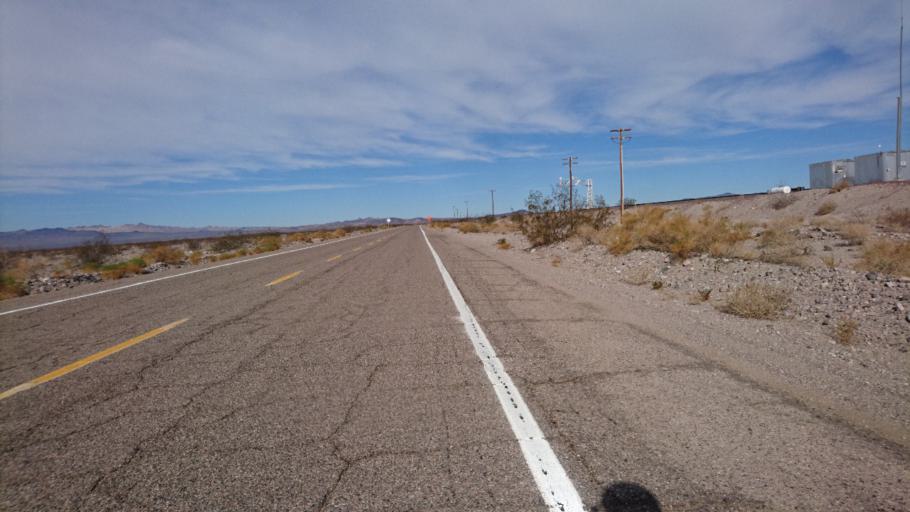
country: US
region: California
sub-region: San Bernardino County
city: Twentynine Palms
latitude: 34.6058
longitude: -115.9621
